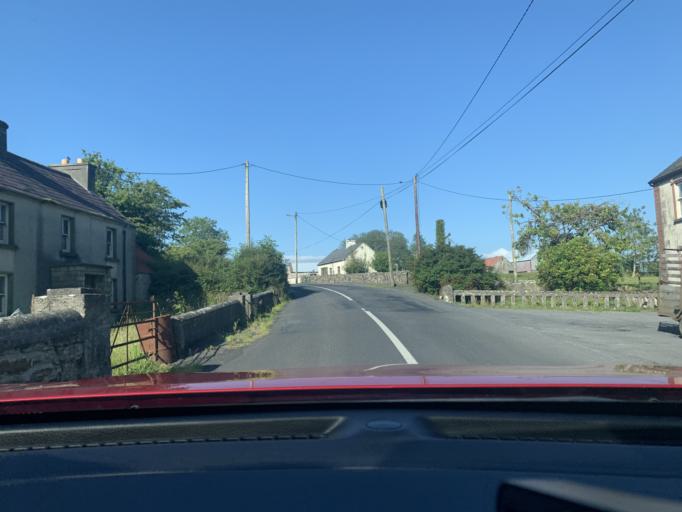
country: IE
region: Connaught
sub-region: Sligo
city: Tobercurry
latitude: 54.1016
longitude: -8.7761
